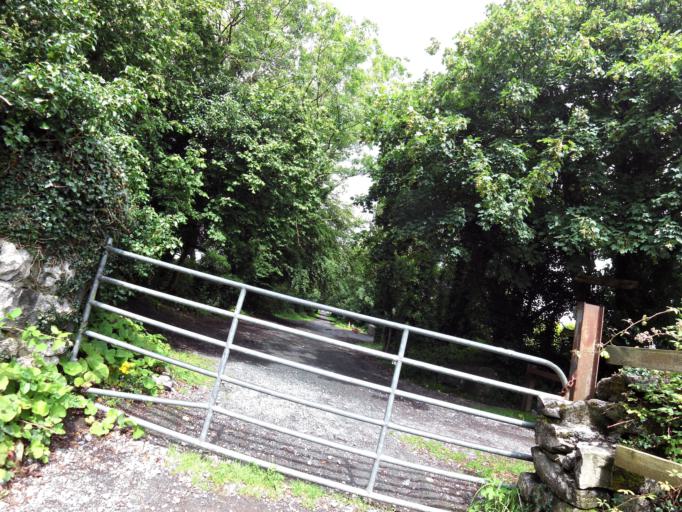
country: IE
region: Connaught
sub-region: County Galway
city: Gaillimh
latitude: 53.2985
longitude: -9.0728
